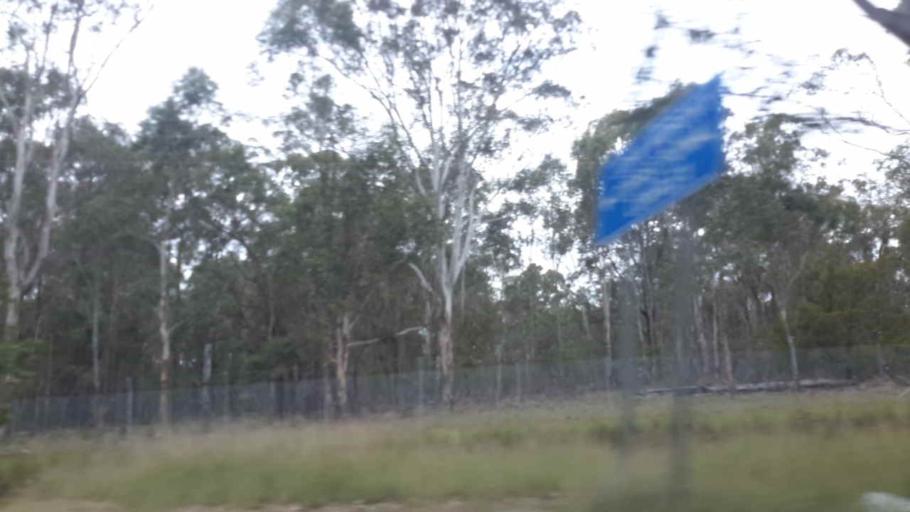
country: AU
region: New South Wales
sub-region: Hawkesbury
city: South Windsor
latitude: -33.6456
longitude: 150.7817
